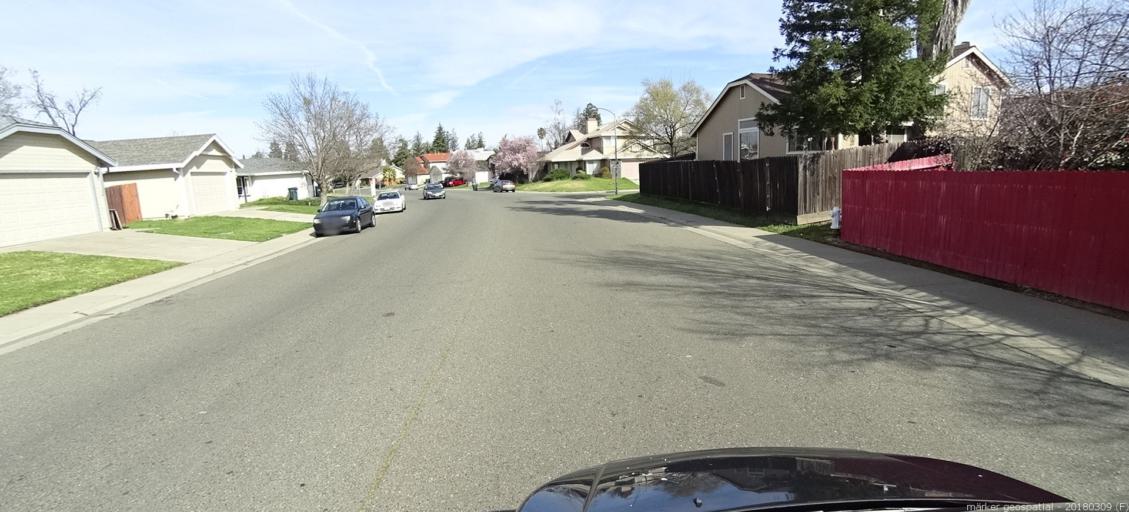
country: US
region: California
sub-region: Sacramento County
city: Florin
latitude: 38.4557
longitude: -121.3953
